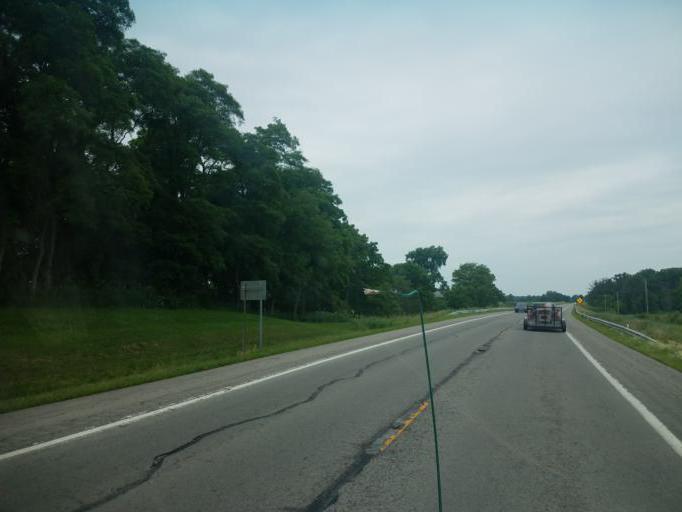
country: US
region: Ohio
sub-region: Hardin County
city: Ada
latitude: 40.7116
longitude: -83.7529
